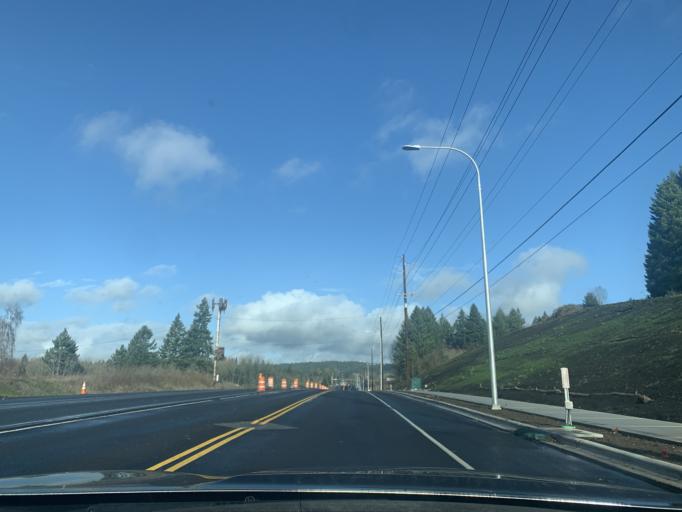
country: US
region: Oregon
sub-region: Washington County
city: King City
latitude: 45.4094
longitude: -122.8516
